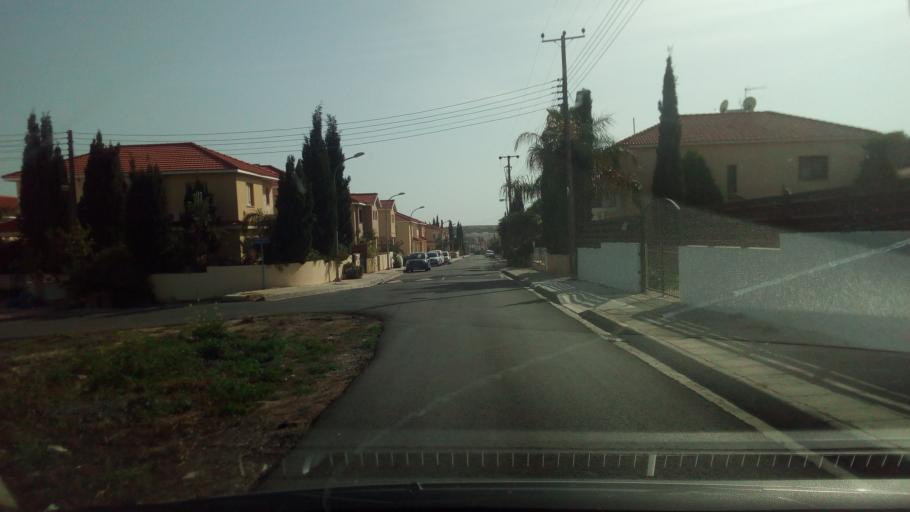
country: CY
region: Larnaka
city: Voroklini
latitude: 34.9801
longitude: 33.6507
